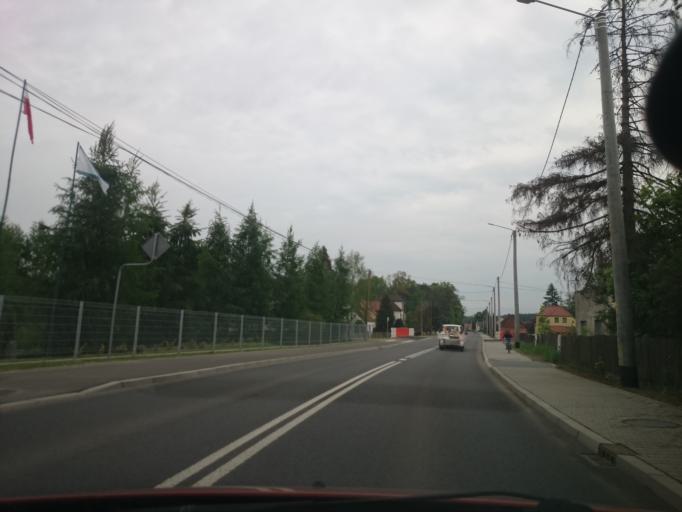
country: PL
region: Opole Voivodeship
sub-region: Powiat opolski
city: Kup
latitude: 50.8116
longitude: 17.8811
